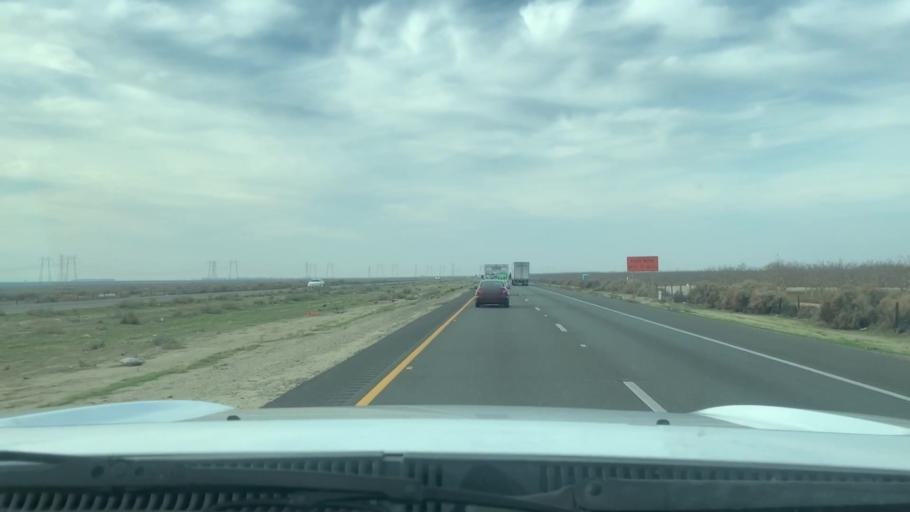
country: US
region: California
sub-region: Kern County
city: Buttonwillow
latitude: 35.4745
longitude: -119.5009
